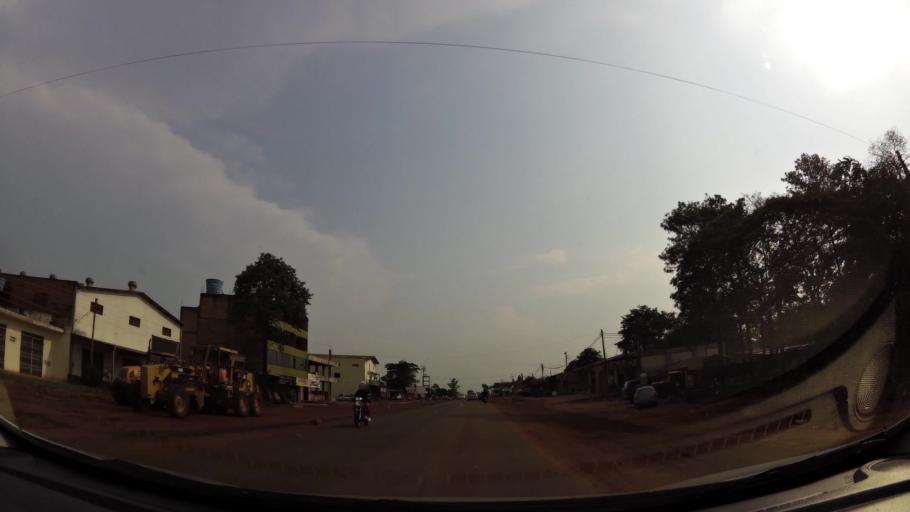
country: PY
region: Alto Parana
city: Ciudad del Este
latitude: -25.4827
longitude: -54.6589
